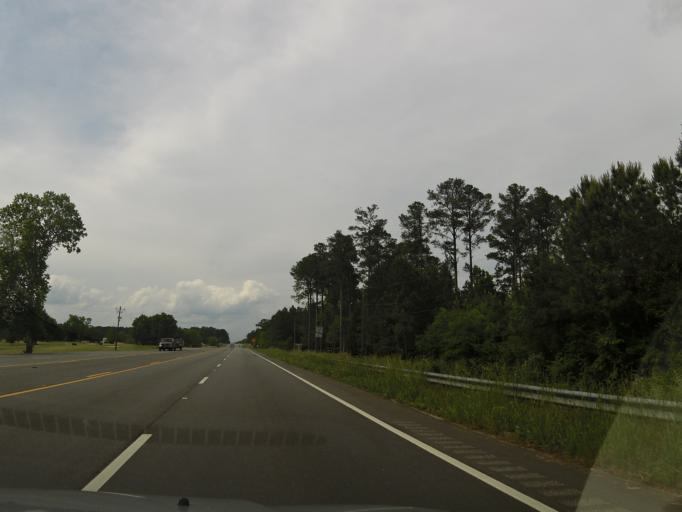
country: US
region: Georgia
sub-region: McDuffie County
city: Thomson
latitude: 33.5323
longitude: -82.5063
